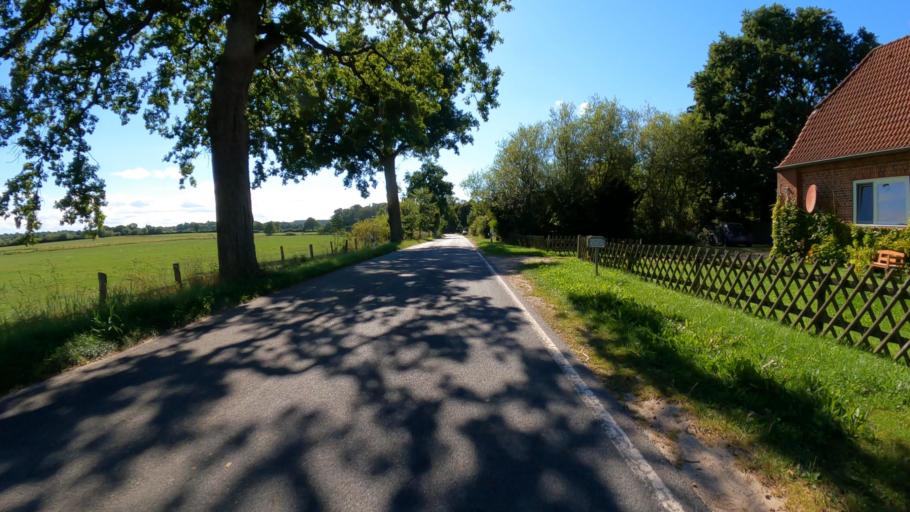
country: DE
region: Schleswig-Holstein
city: Westerau
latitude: 53.7683
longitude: 10.5144
